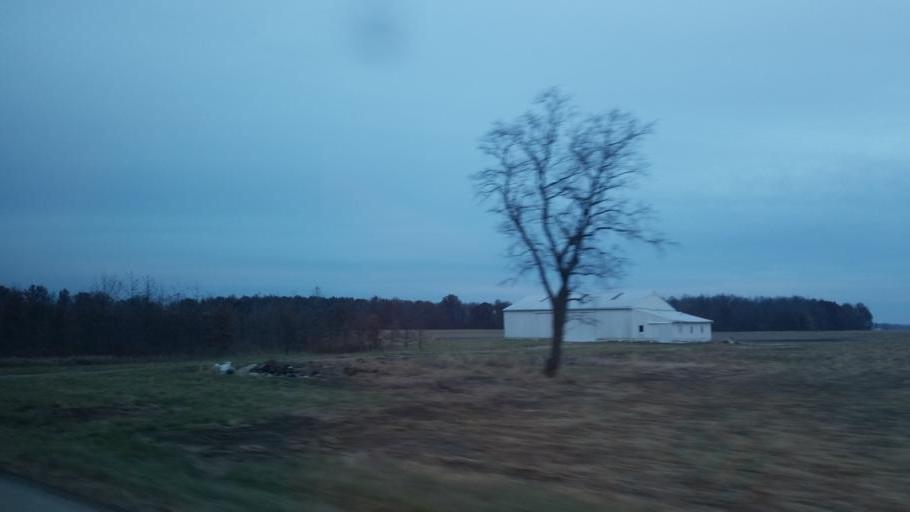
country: US
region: Indiana
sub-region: Adams County
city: Decatur
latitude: 40.7617
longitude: -85.0140
